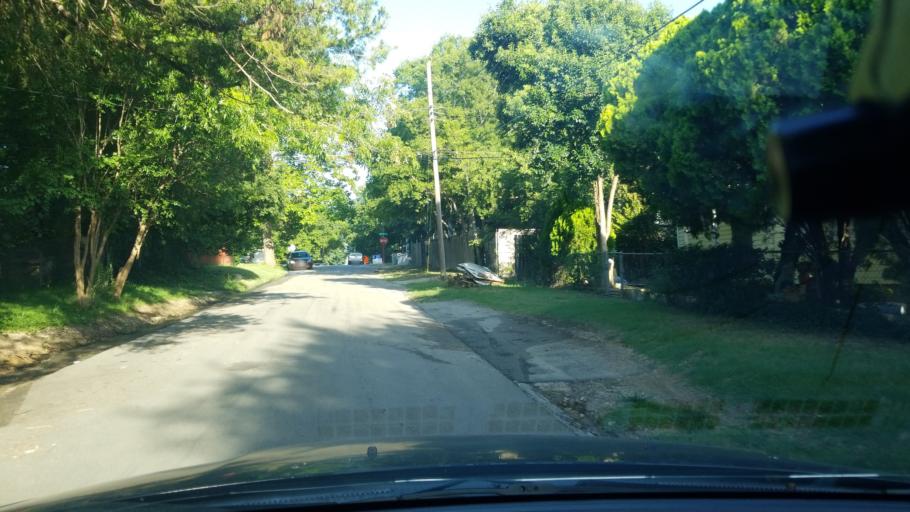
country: US
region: Texas
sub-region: Dallas County
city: Dallas
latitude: 32.7215
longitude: -96.8195
